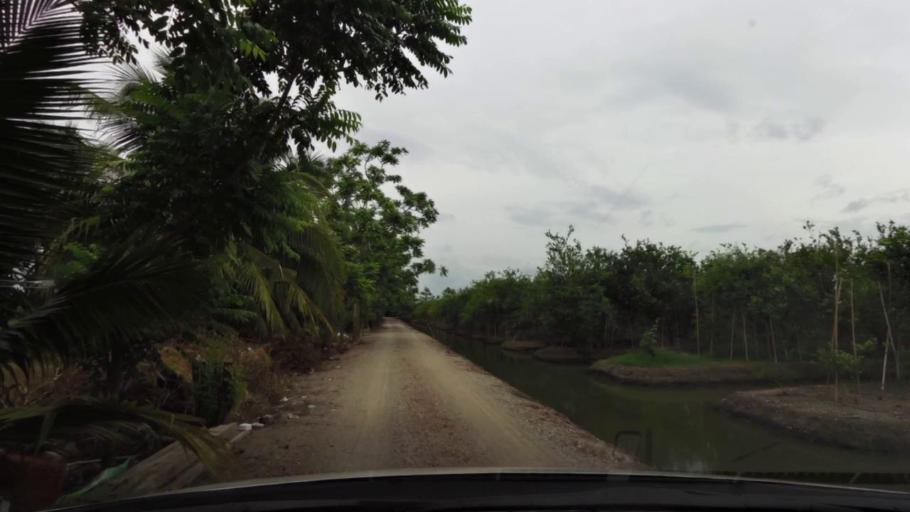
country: TH
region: Ratchaburi
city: Damnoen Saduak
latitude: 13.5577
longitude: 100.0082
